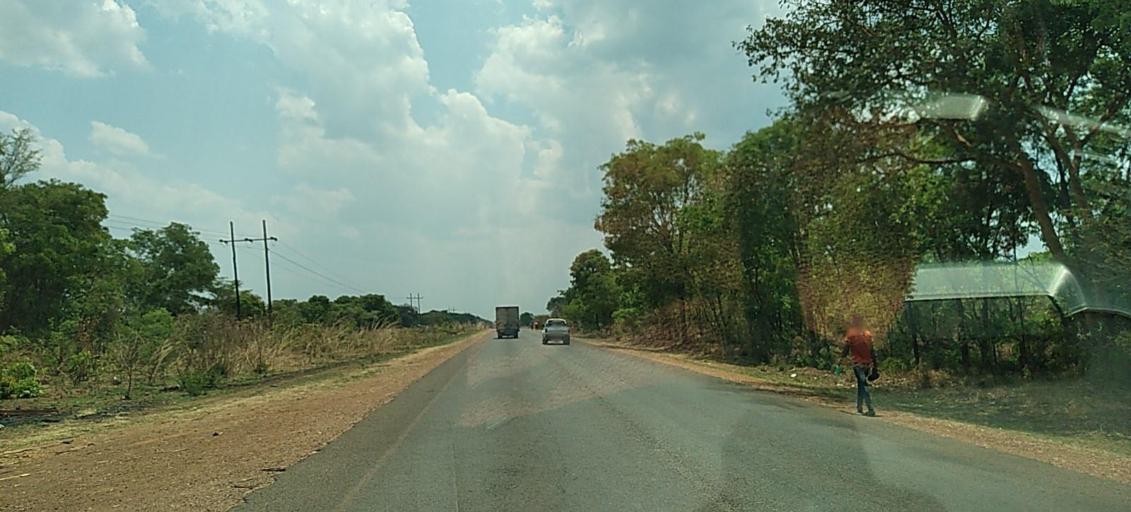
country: ZM
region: Copperbelt
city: Kalulushi
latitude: -12.8353
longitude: 27.9575
